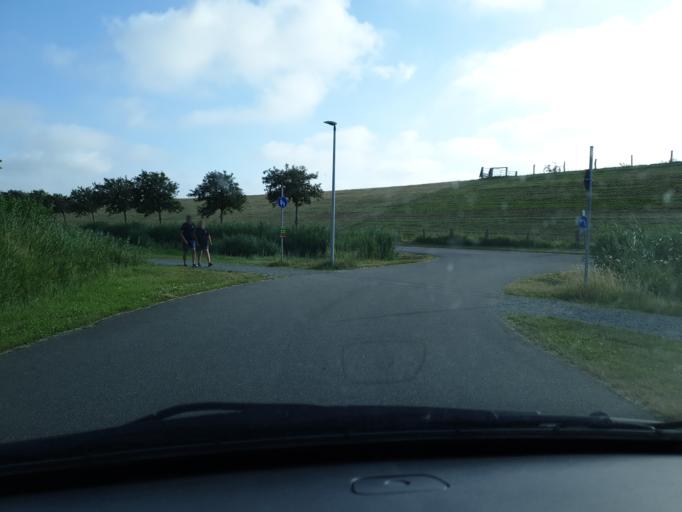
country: DE
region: Schleswig-Holstein
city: Friedrichskoog
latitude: 54.0278
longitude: 8.8384
